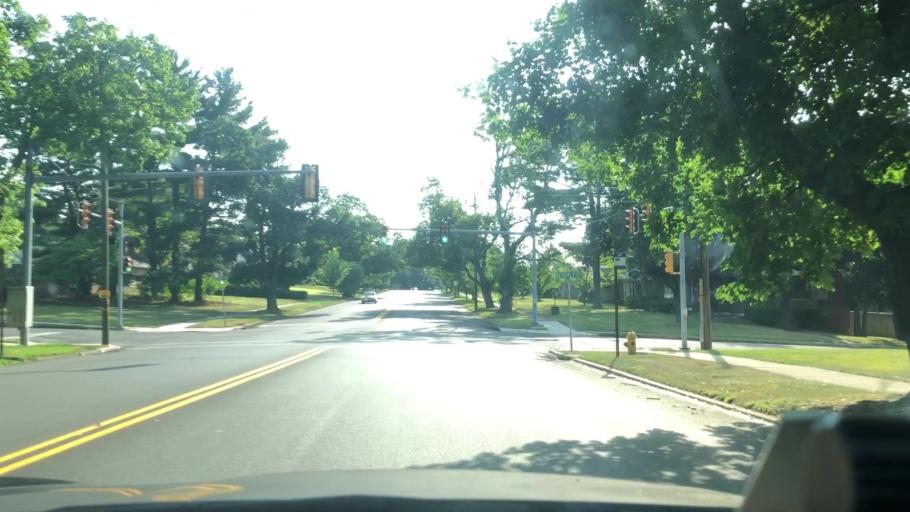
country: US
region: Pennsylvania
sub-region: Lehigh County
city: Fountain Hill
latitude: 40.6280
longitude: -75.4118
